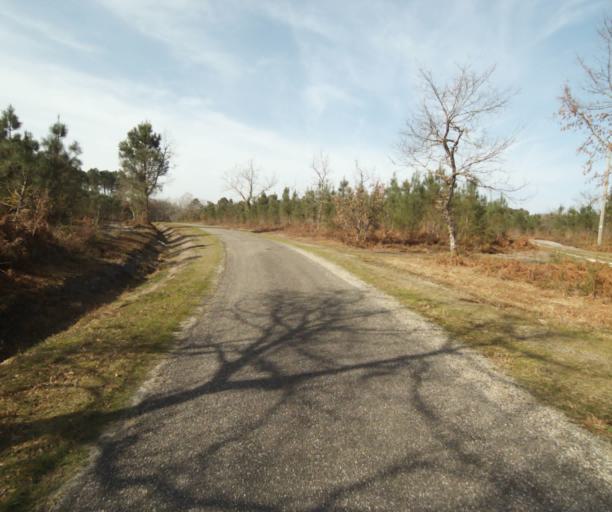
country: FR
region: Aquitaine
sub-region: Departement des Landes
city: Roquefort
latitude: 44.1346
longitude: -0.1948
